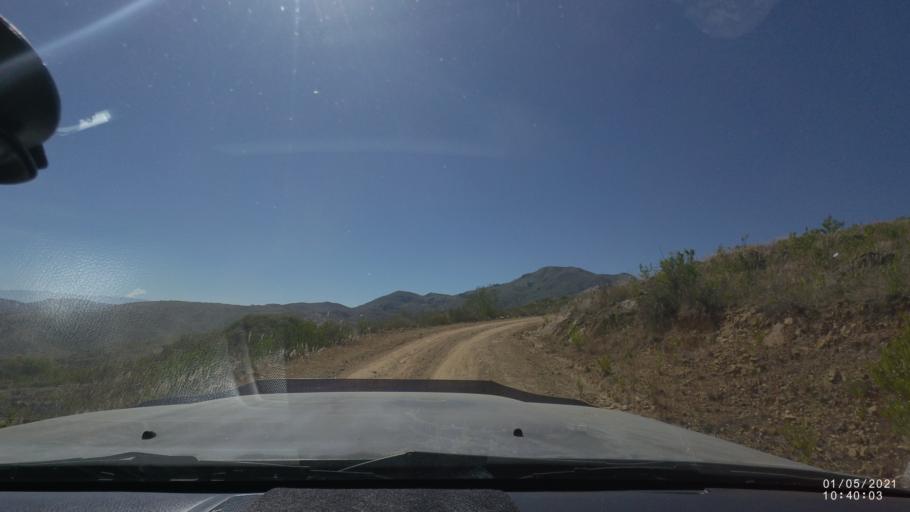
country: BO
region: Cochabamba
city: Capinota
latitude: -17.6060
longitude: -66.1835
